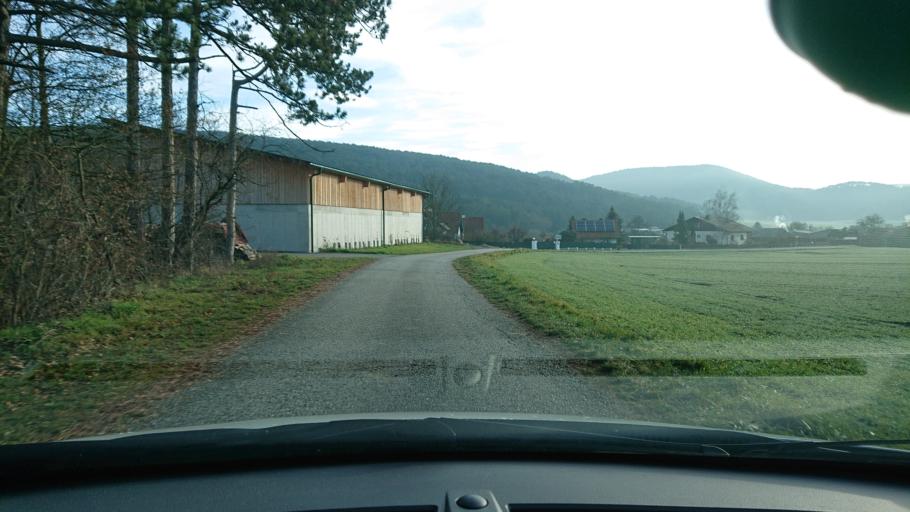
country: AT
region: Lower Austria
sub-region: Politischer Bezirk Baden
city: Berndorf
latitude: 47.9291
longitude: 16.1096
